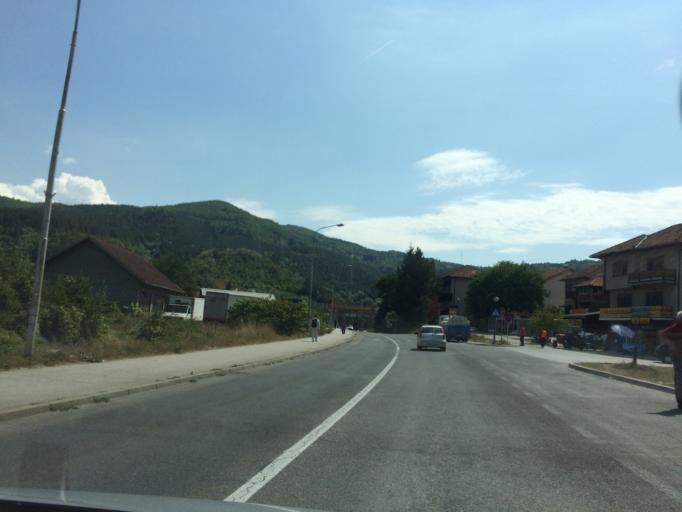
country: RS
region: Central Serbia
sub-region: Zlatiborski Okrug
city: Prijepolje
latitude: 43.3917
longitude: 19.6408
